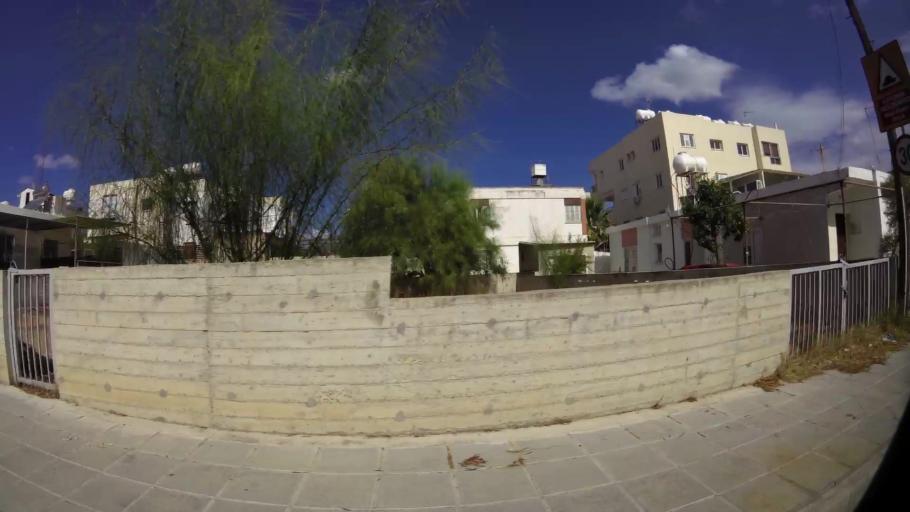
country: CY
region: Lefkosia
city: Nicosia
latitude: 35.1507
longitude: 33.3657
